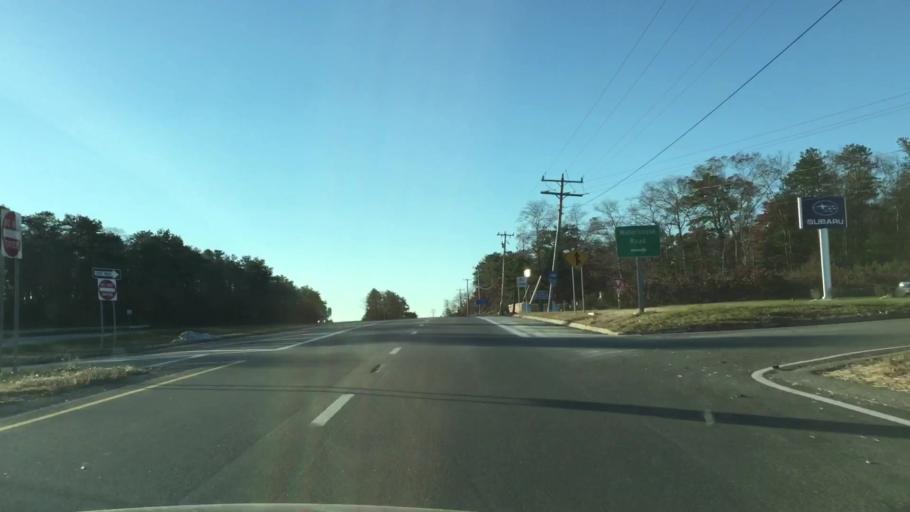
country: US
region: Massachusetts
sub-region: Barnstable County
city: Bourne
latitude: 41.7267
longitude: -70.5846
